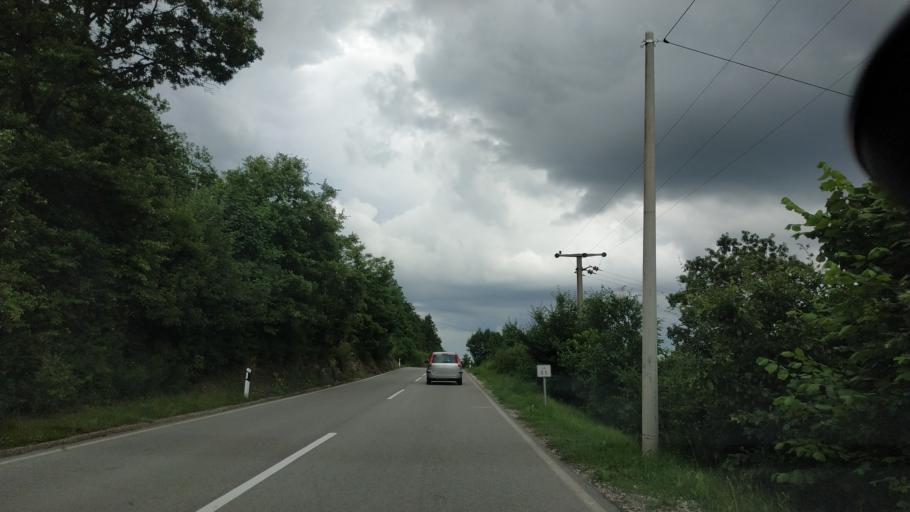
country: RS
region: Central Serbia
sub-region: Borski Okrug
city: Bor
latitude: 44.0497
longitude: 22.0749
